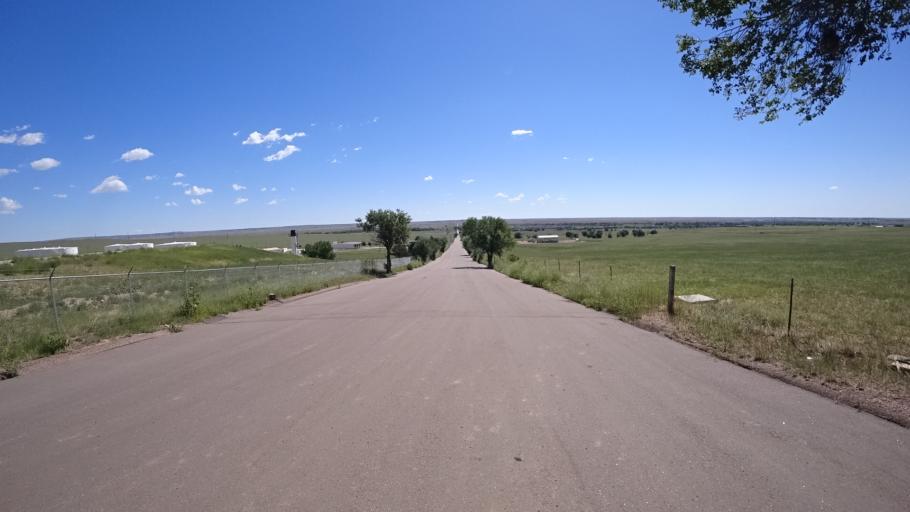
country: US
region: Colorado
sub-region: El Paso County
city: Security-Widefield
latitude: 38.7809
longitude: -104.6803
